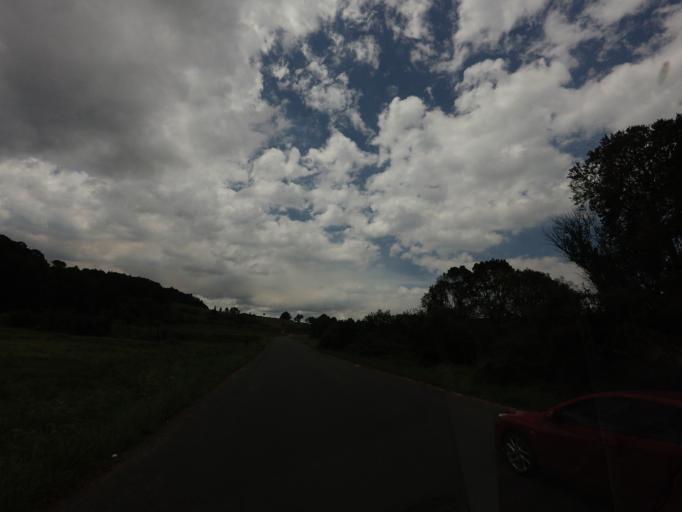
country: ZA
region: Mpumalanga
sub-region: Ehlanzeni District
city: Graksop
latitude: -24.9877
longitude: 30.8119
